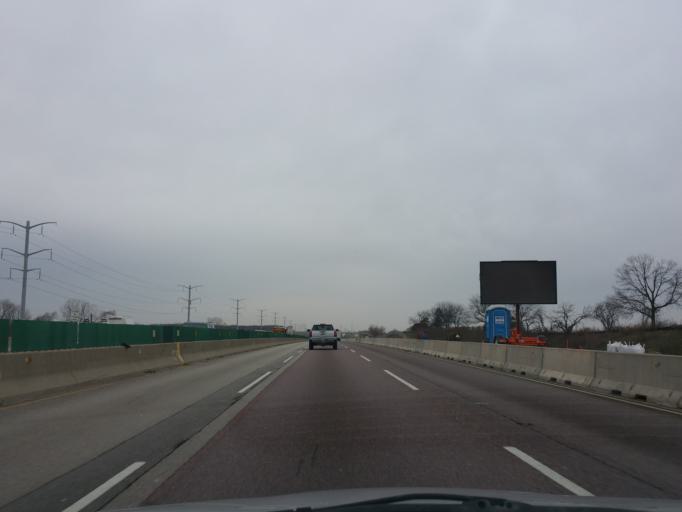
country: US
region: Illinois
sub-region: Cook County
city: Streamwood
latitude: 42.0666
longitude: -88.1695
